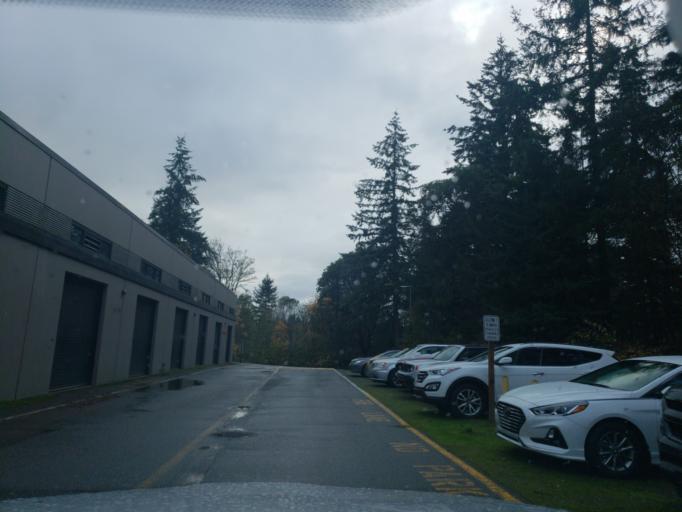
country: US
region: Washington
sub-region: King County
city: Shoreline
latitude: 47.7498
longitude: -122.3626
